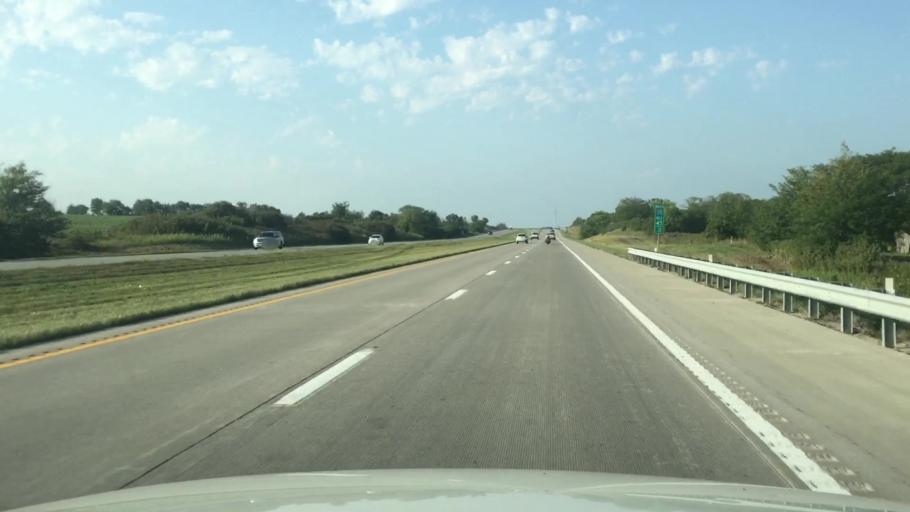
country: US
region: Missouri
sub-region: Clinton County
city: Lathrop
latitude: 39.6217
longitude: -94.2473
